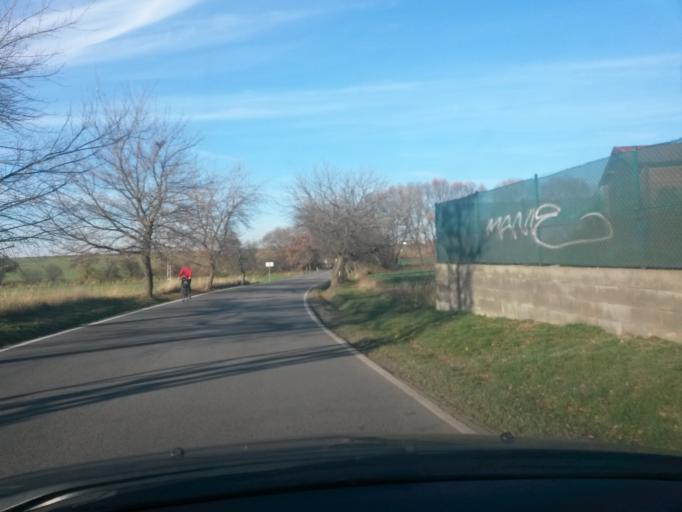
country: CZ
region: Central Bohemia
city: Jesenice
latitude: 49.9526
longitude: 14.5182
